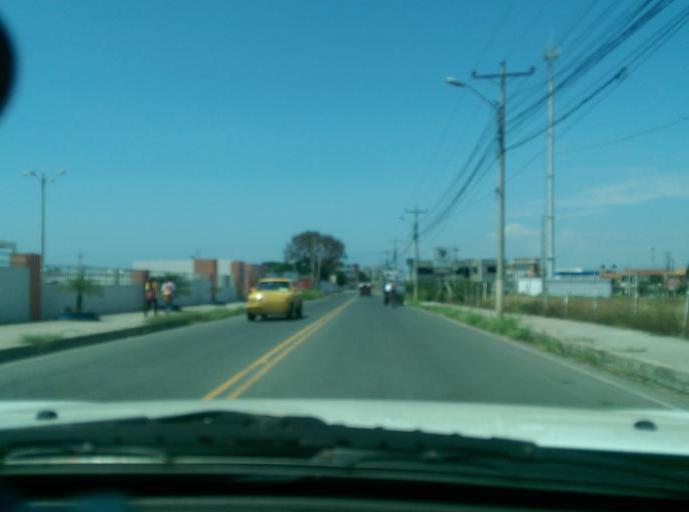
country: EC
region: Manabi
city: Manta
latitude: -0.9583
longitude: -80.7577
